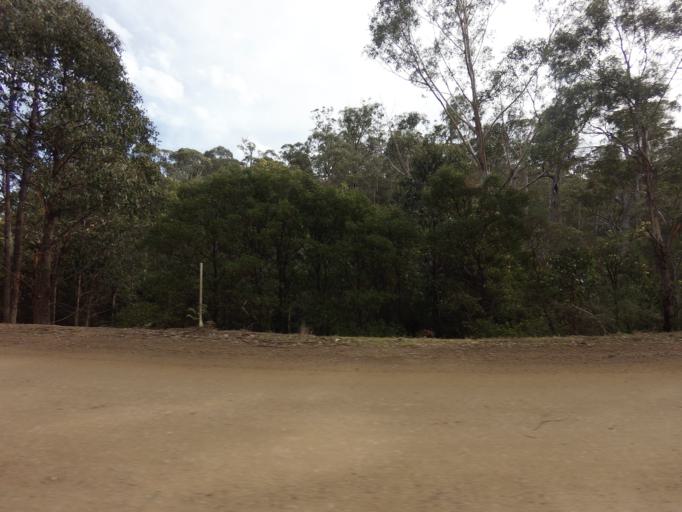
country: AU
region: Tasmania
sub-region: Huon Valley
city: Huonville
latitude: -43.0672
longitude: 147.0887
